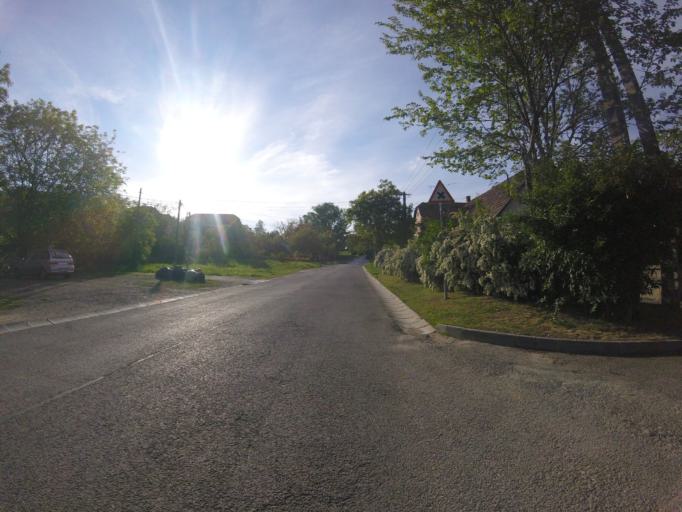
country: HU
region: Pest
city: Budakalasz
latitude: 47.6012
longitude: 19.0369
